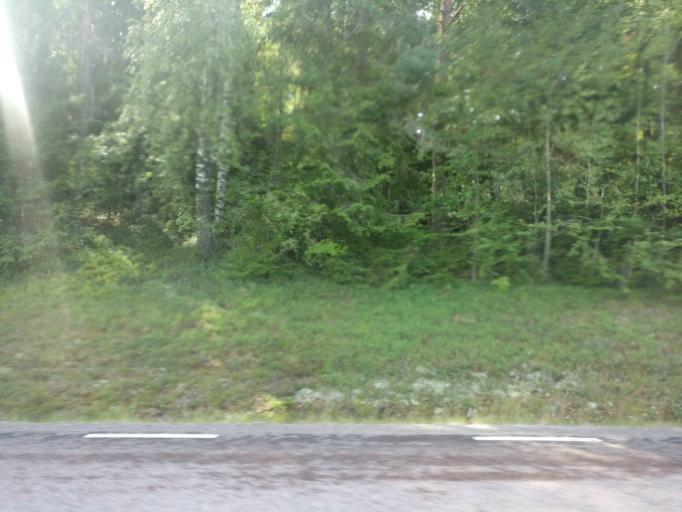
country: SE
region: Vaermland
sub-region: Hagfors Kommun
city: Ekshaerad
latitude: 60.2789
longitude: 13.4106
